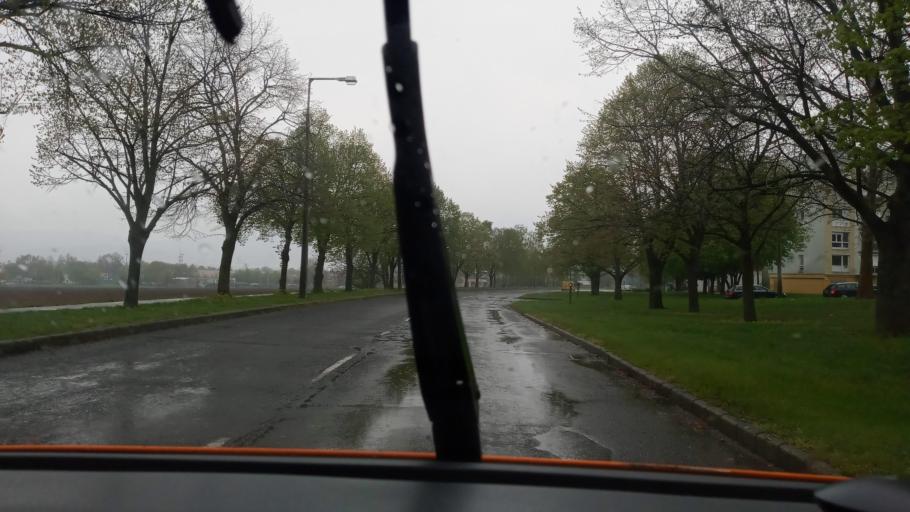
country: HU
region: Baranya
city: Pecs
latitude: 46.0316
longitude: 18.2125
